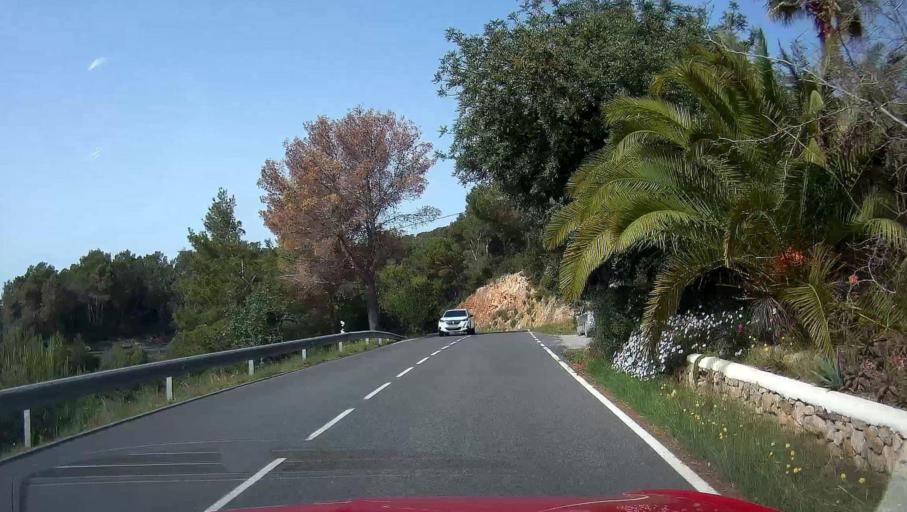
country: ES
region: Balearic Islands
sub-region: Illes Balears
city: Sant Joan de Labritja
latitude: 39.0603
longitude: 1.5828
